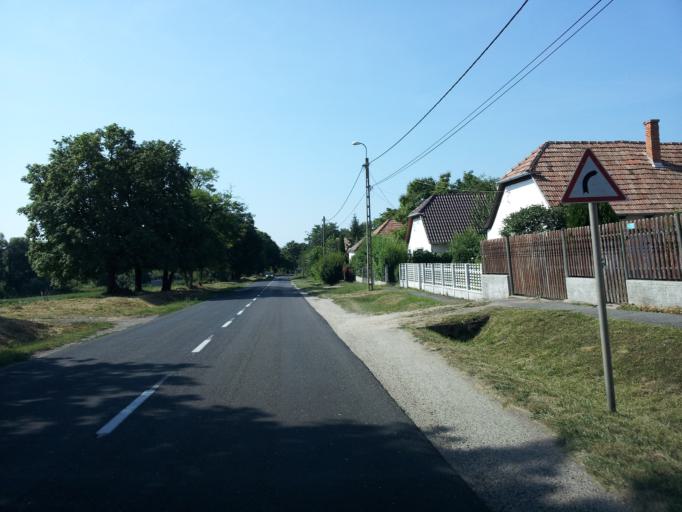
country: HU
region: Fejer
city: Lovasbereny
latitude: 47.3588
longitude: 18.5810
